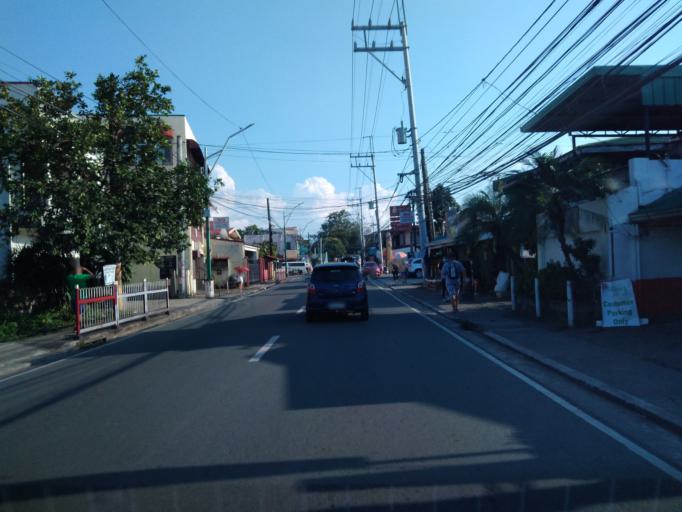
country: PH
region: Calabarzon
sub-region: Province of Laguna
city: Los Banos
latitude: 14.1758
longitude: 121.2429
